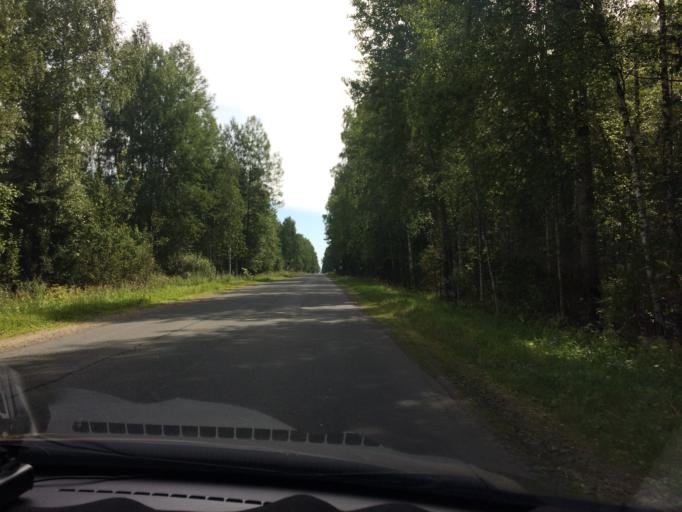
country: RU
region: Mariy-El
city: Surok
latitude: 56.5706
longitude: 48.2231
